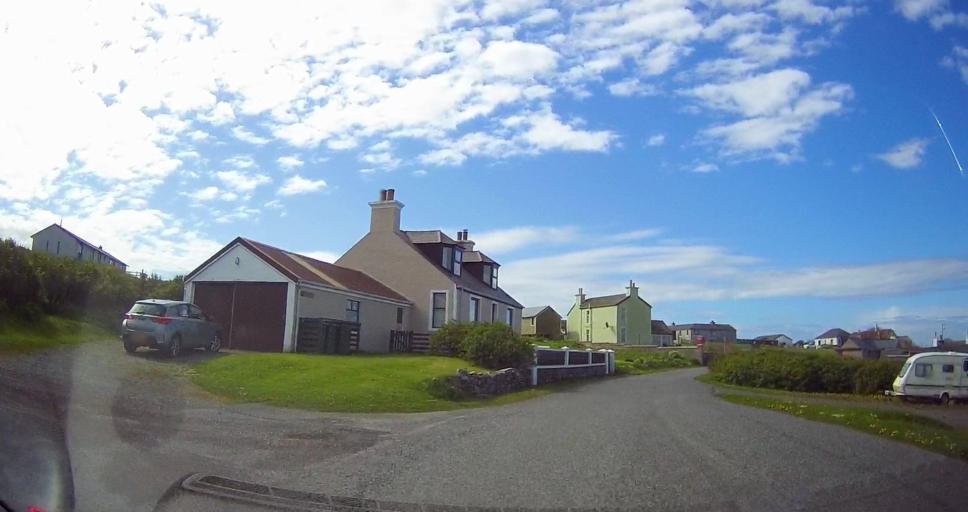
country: GB
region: Scotland
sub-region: Shetland Islands
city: Sandwick
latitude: 59.9742
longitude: -1.3228
